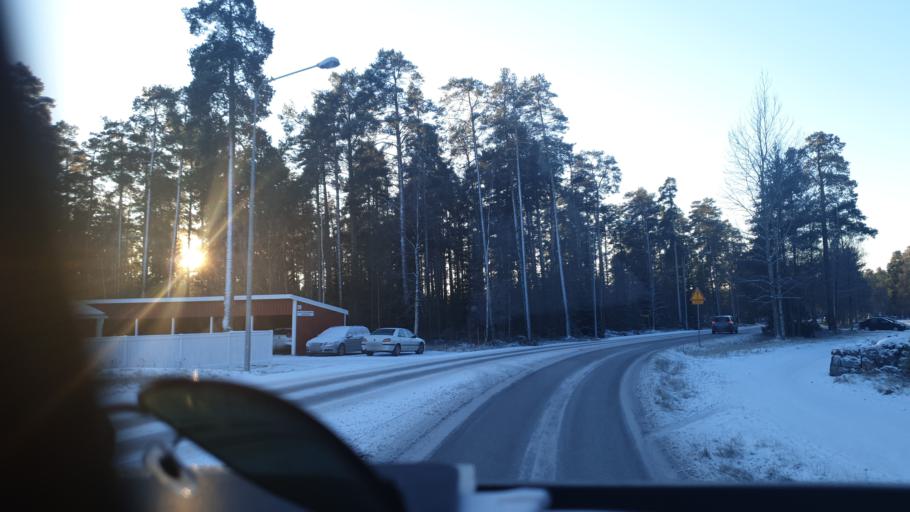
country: FI
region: Central Ostrobothnia
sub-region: Kokkola
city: Kokkola
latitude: 63.8291
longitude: 23.1030
